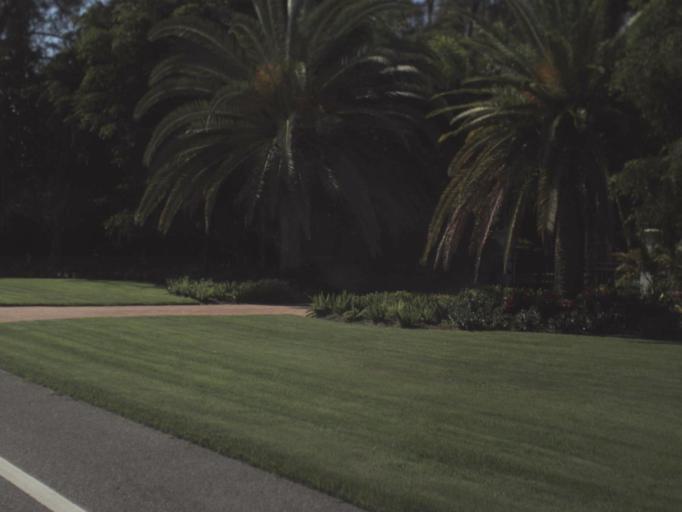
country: US
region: Florida
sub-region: Manatee County
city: Longboat Key
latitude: 27.4195
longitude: -82.6660
